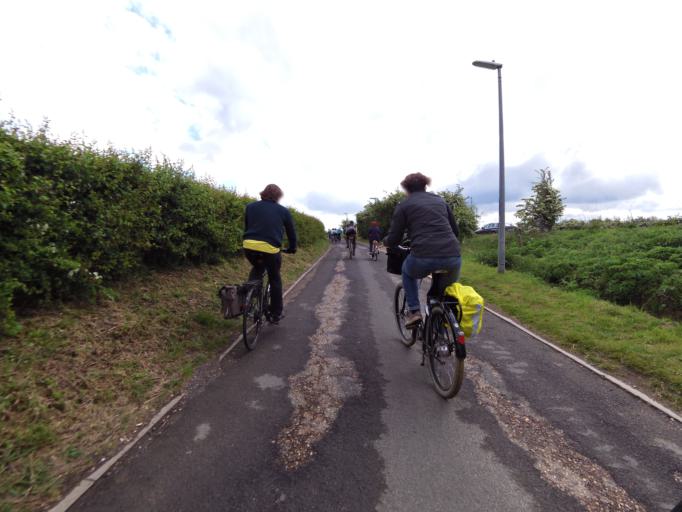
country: GB
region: England
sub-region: Cambridgeshire
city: Fulbourn
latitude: 52.2144
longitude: 0.2095
